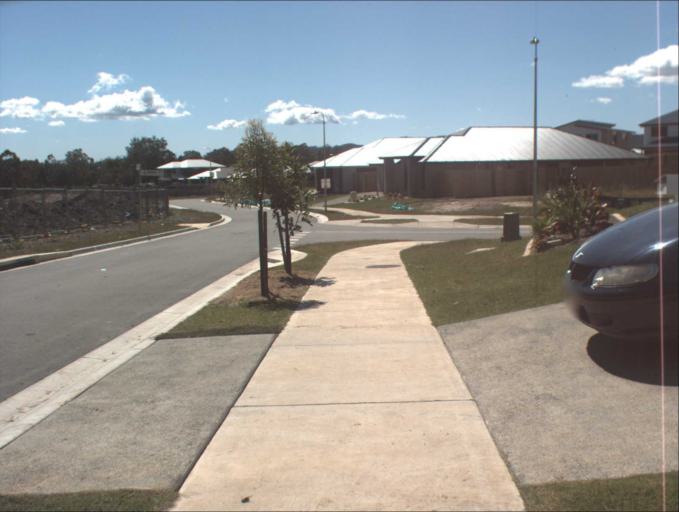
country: AU
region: Queensland
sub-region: Logan
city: Chambers Flat
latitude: -27.7969
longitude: 153.1024
